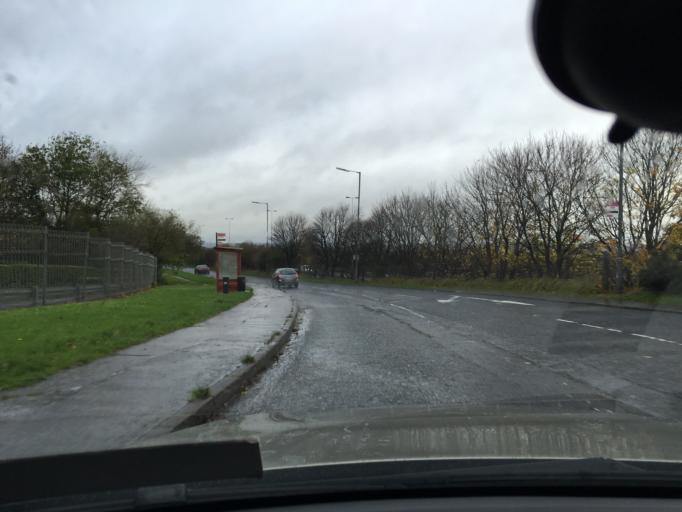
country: GB
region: Northern Ireland
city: Carnmoney
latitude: 54.6690
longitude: -5.9647
